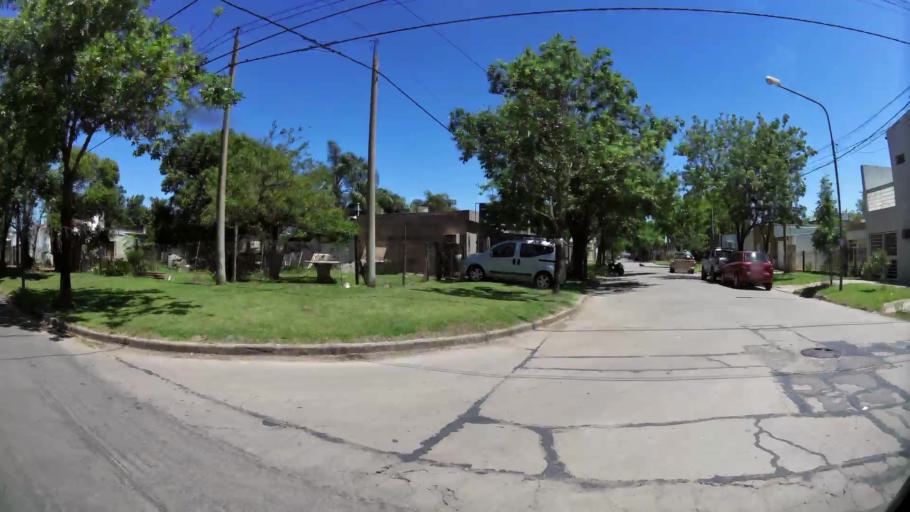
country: AR
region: Santa Fe
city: Rafaela
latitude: -31.2495
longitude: -61.4596
